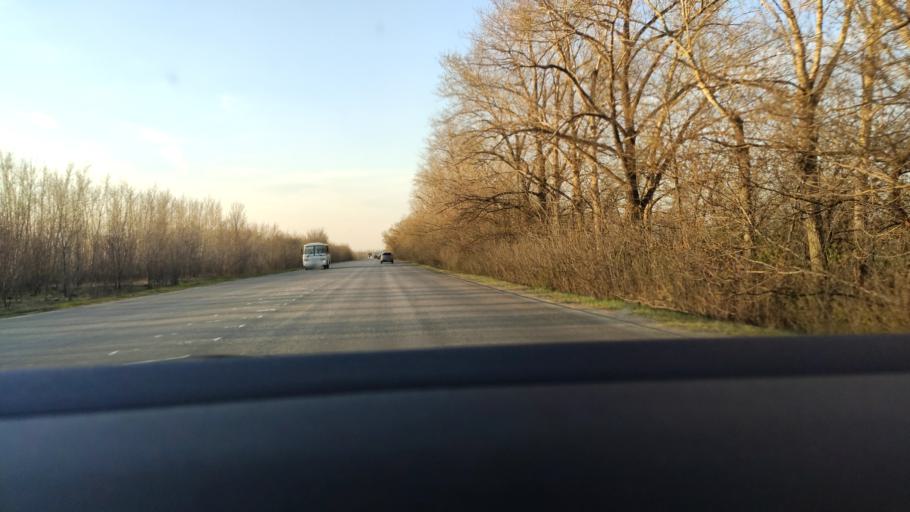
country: RU
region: Voronezj
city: Maslovka
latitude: 51.4885
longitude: 39.3078
